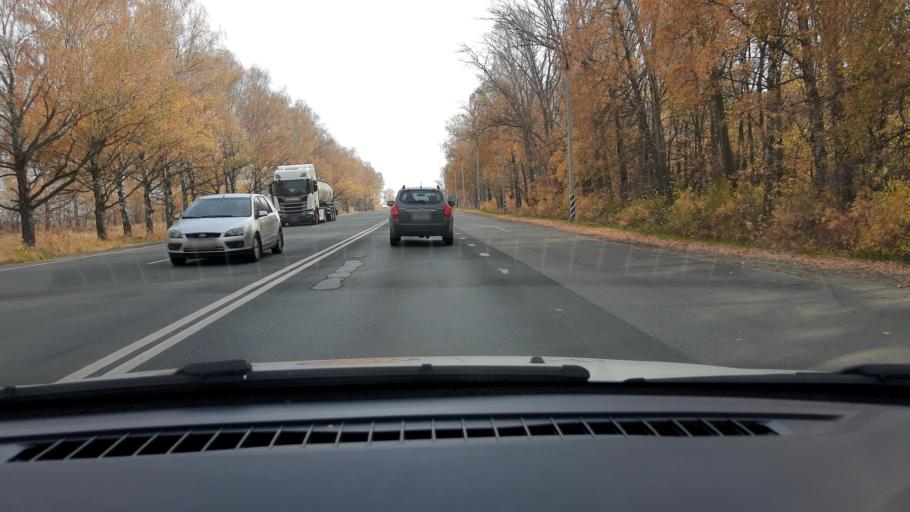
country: RU
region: Nizjnij Novgorod
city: Kstovo
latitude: 56.1362
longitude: 44.2396
